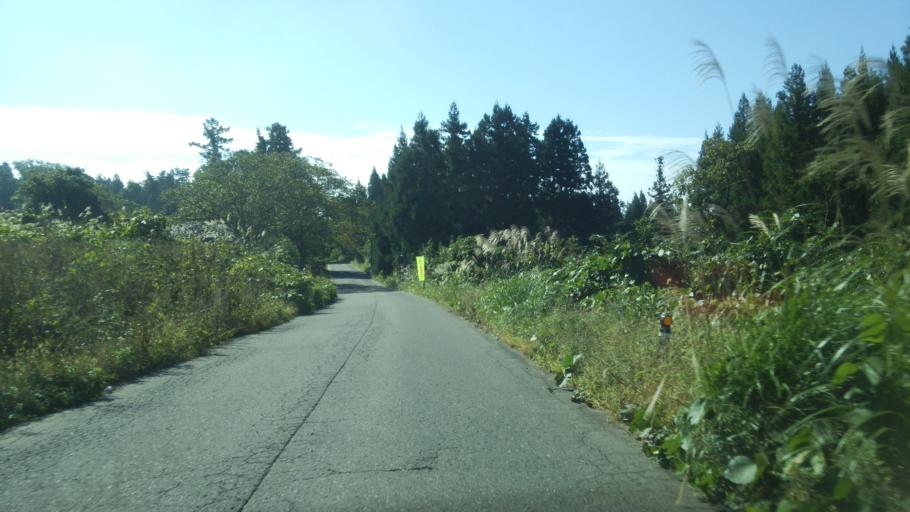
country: JP
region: Fukushima
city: Kitakata
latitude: 37.6055
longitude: 139.9407
